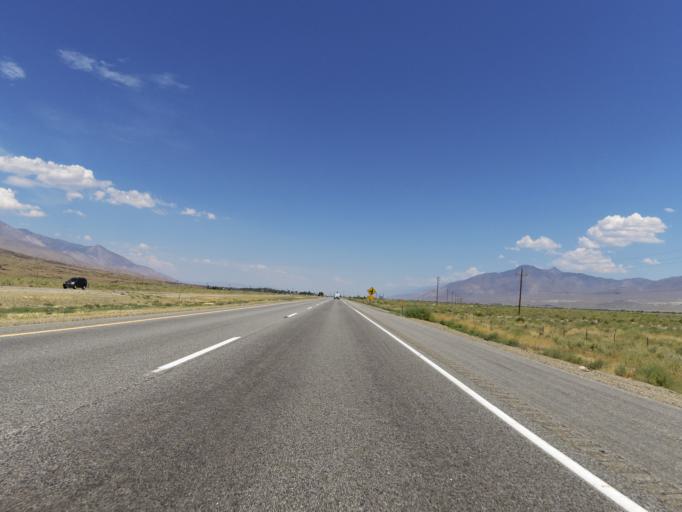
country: US
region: California
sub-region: Inyo County
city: Big Pine
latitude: 37.1013
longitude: -118.2513
